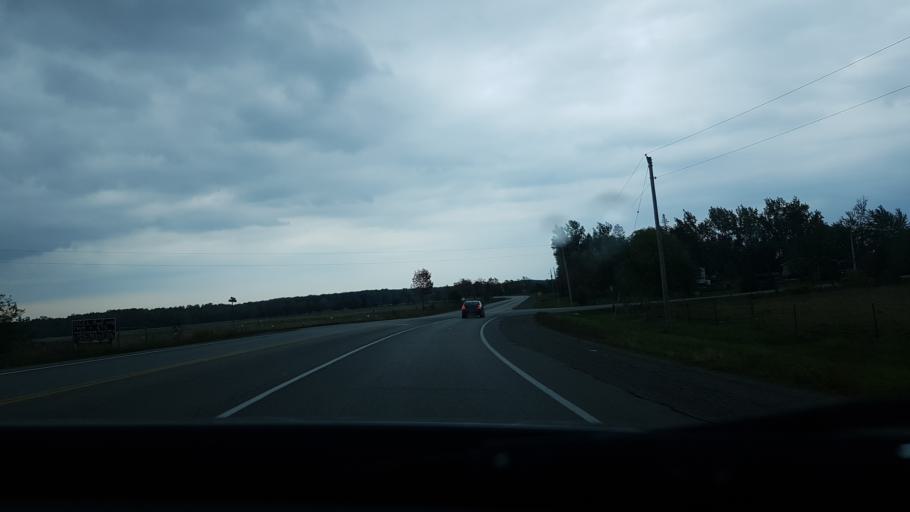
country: CA
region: Ontario
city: Omemee
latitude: 44.3765
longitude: -78.6422
